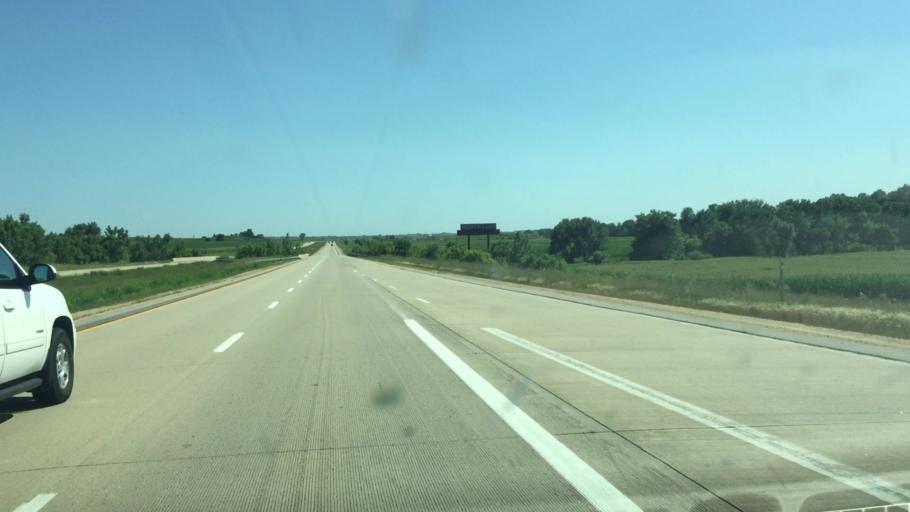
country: US
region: Iowa
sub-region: Jones County
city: Monticello
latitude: 42.2258
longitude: -91.1721
